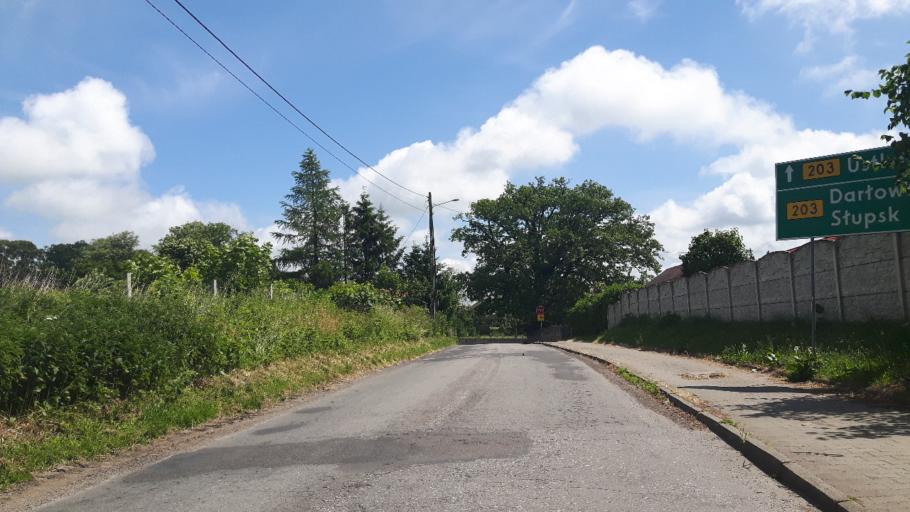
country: PL
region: Pomeranian Voivodeship
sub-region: Powiat slupski
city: Ustka
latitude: 54.5211
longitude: 16.7640
